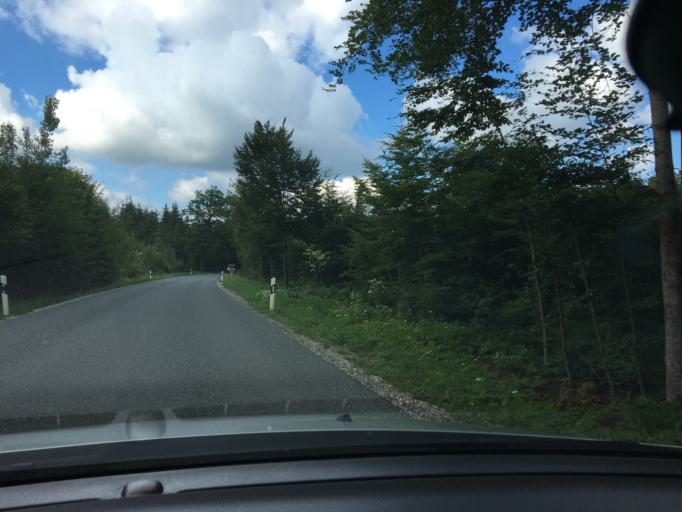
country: DE
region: Bavaria
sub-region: Upper Bavaria
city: Otterfing
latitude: 47.9260
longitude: 11.6538
